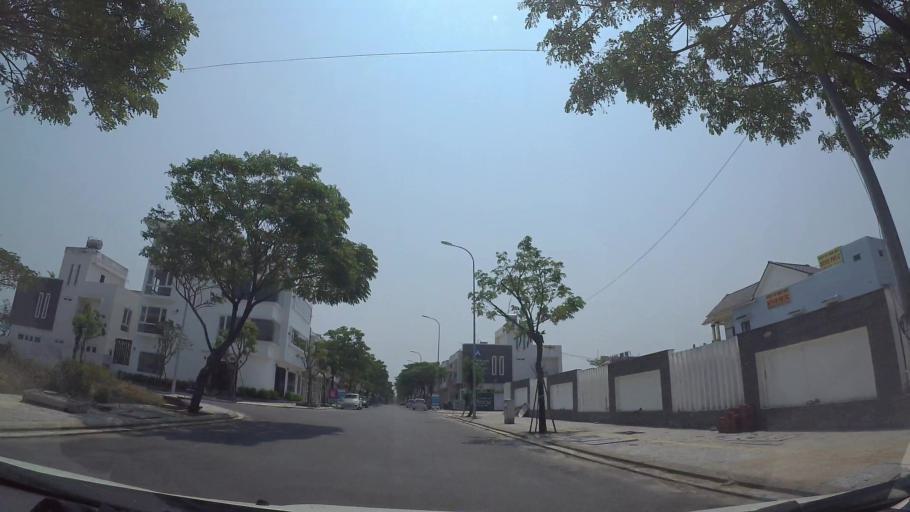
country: VN
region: Da Nang
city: Ngu Hanh Son
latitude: 15.9776
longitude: 108.2610
